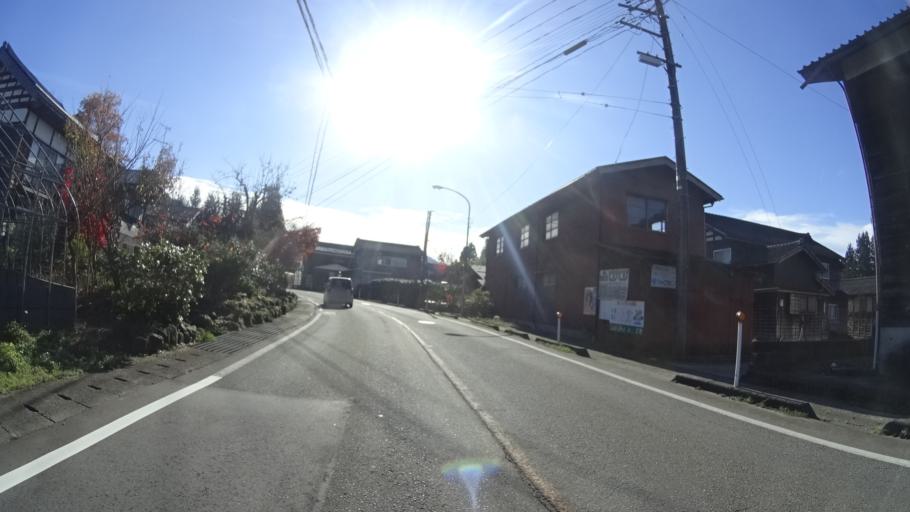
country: JP
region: Niigata
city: Tochio-honcho
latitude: 37.4900
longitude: 138.9743
